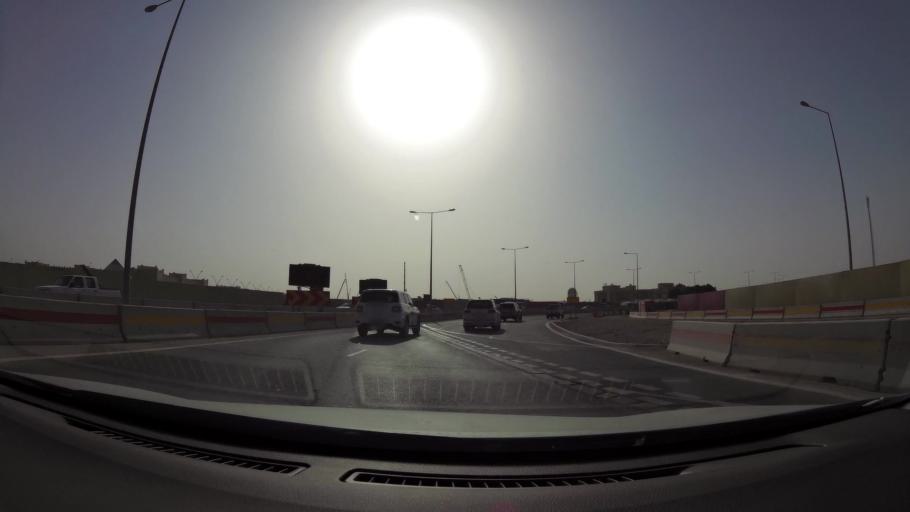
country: QA
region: Baladiyat ar Rayyan
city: Ar Rayyan
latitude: 25.3178
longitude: 51.4307
